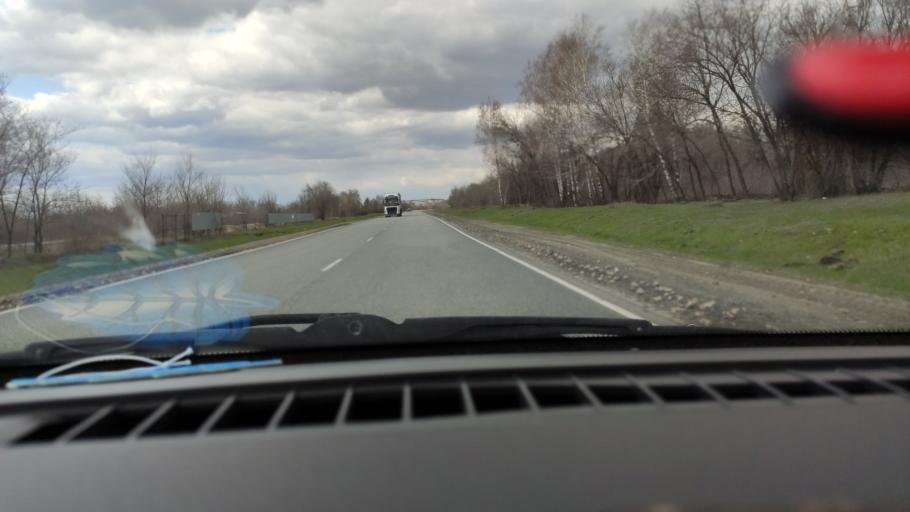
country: RU
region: Saratov
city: Tersa
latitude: 52.0826
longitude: 47.5692
